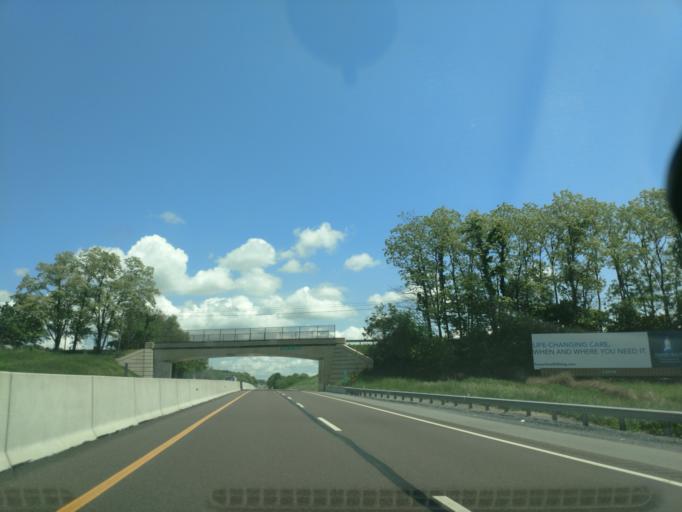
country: US
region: Pennsylvania
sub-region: Lancaster County
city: Schoeneck
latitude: 40.2458
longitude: -76.2009
